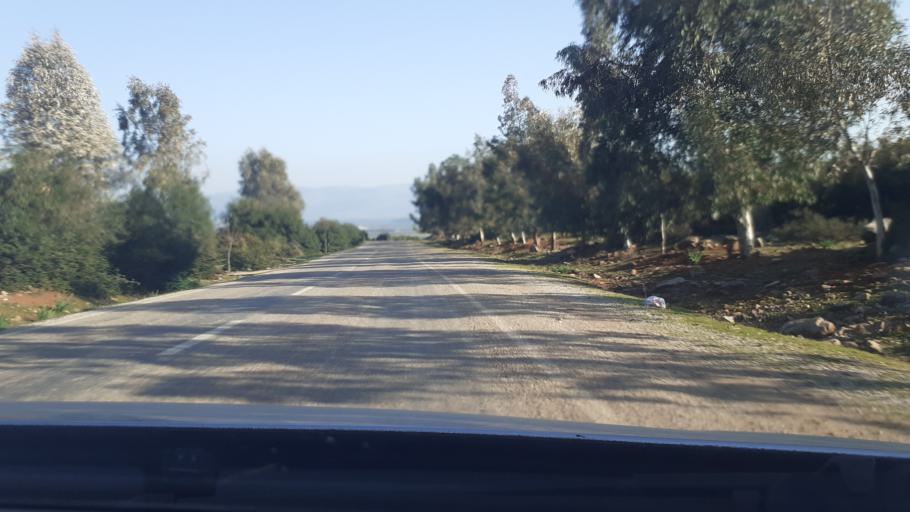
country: TR
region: Hatay
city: Aktepe
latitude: 36.7303
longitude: 36.4808
